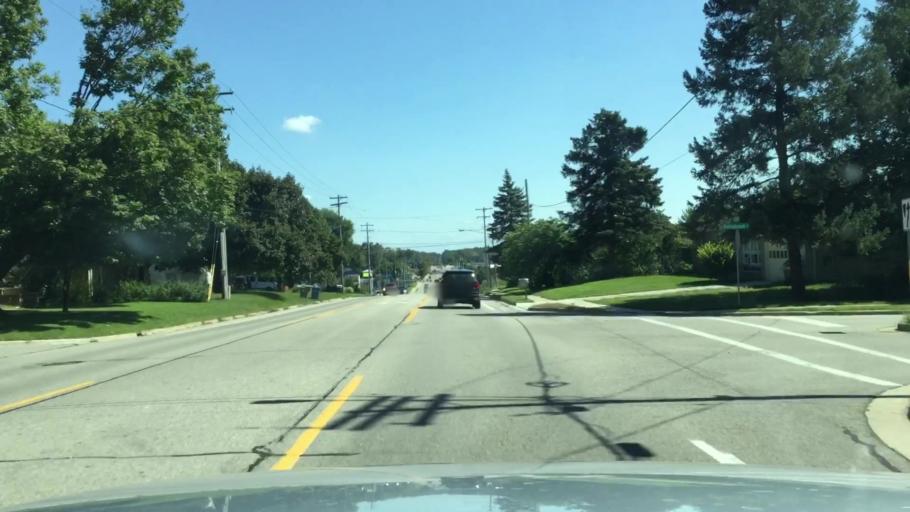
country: US
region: Michigan
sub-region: Kalamazoo County
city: Portage
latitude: 42.2155
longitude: -85.5988
